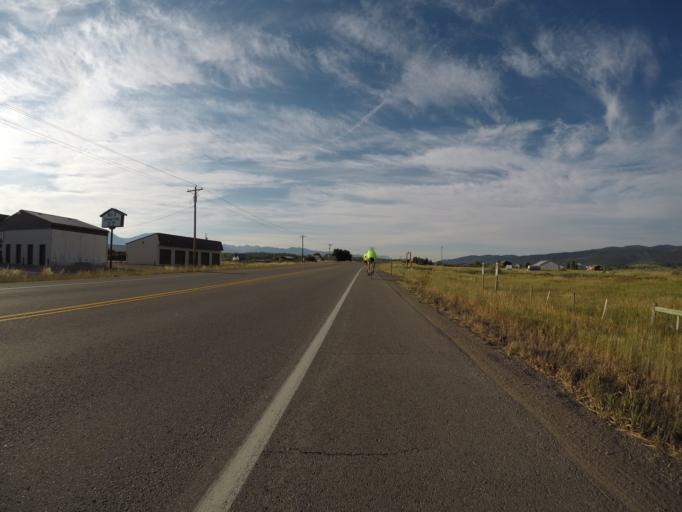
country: US
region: Wyoming
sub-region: Lincoln County
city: Afton
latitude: 42.9454
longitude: -111.0082
